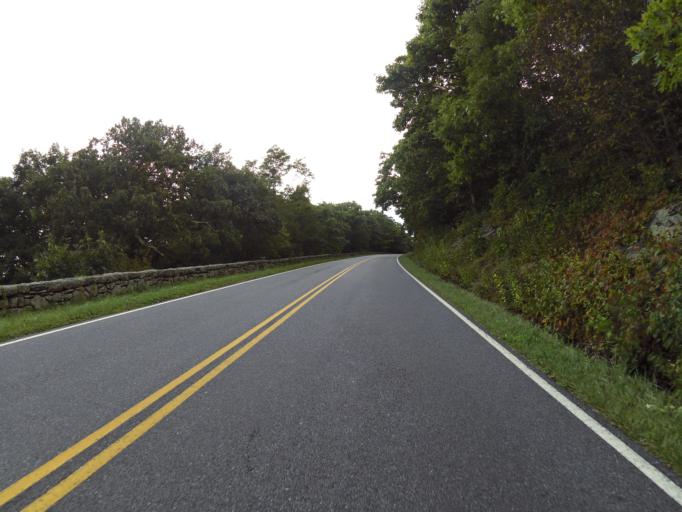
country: US
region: Virginia
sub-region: Page County
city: Stanley
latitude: 38.5671
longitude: -78.3794
